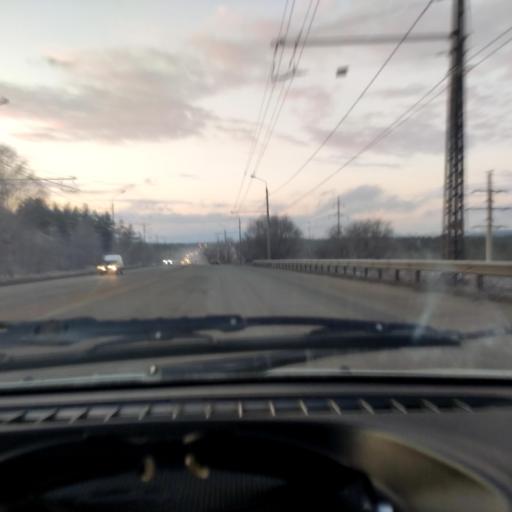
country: RU
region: Samara
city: Zhigulevsk
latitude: 53.5074
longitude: 49.5181
